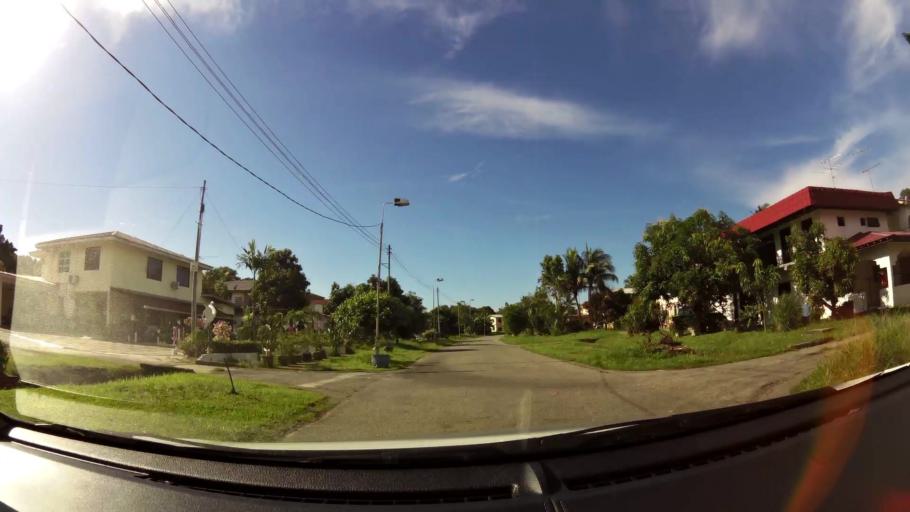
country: BN
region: Brunei and Muara
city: Bandar Seri Begawan
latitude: 4.9650
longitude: 114.9529
